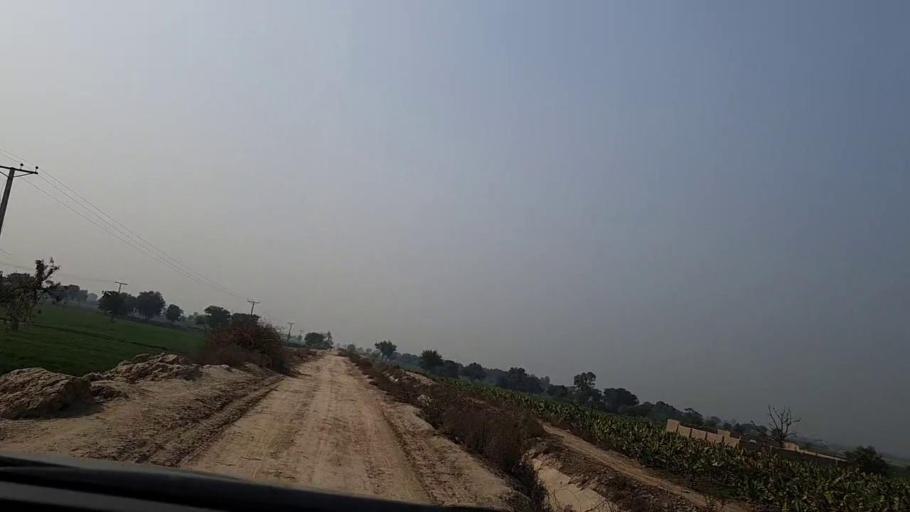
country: PK
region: Sindh
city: Sakrand
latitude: 26.1391
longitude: 68.2285
